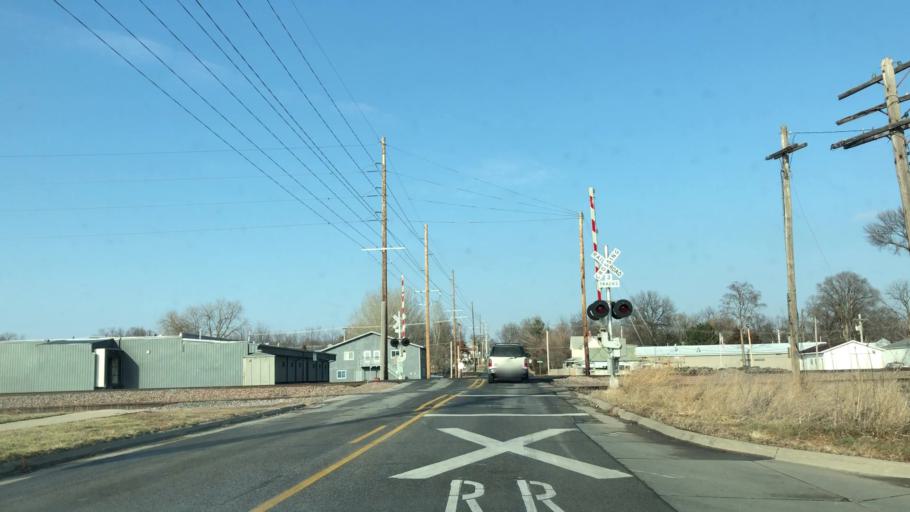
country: US
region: Iowa
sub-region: Marshall County
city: Marshalltown
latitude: 42.0392
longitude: -92.9224
